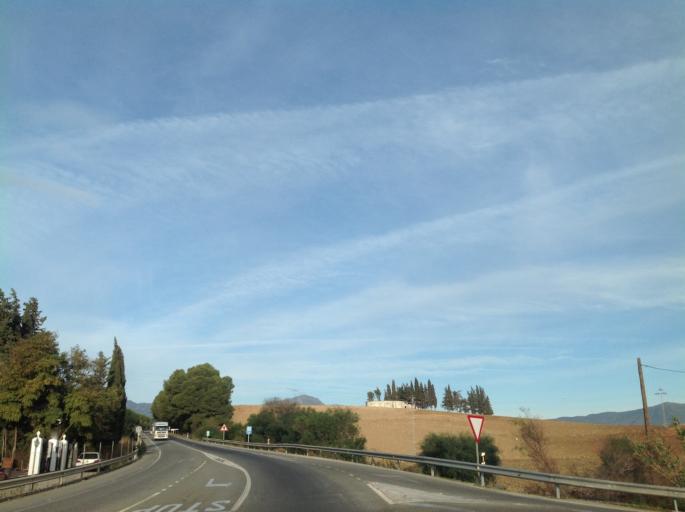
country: ES
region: Andalusia
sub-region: Provincia de Malaga
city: Pizarra
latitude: 36.7472
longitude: -4.7120
